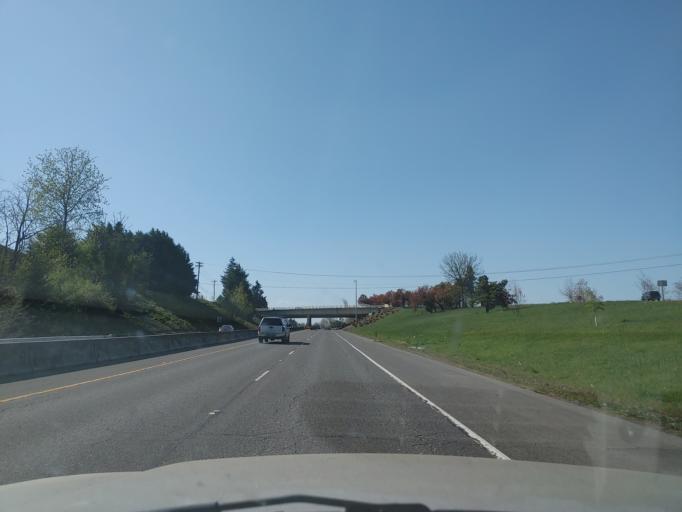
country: US
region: Oregon
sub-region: Clackamas County
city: Oatfield
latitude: 45.4291
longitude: -122.6039
